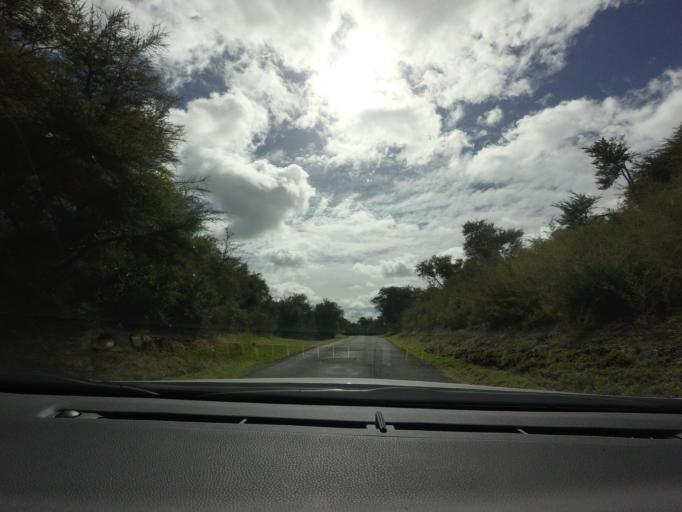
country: NZ
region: Bay of Plenty
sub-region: Rotorua District
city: Rotorua
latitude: -38.3501
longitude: 176.3705
